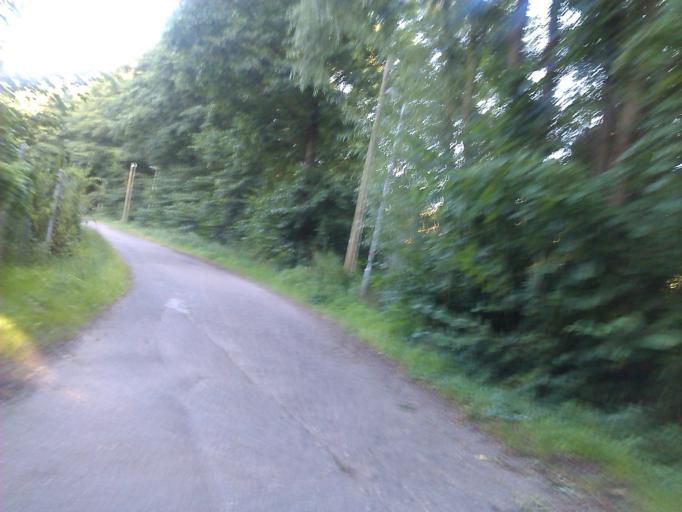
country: DE
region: Baden-Wuerttemberg
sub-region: Karlsruhe Region
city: Muhlhausen
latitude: 49.2496
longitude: 8.7366
